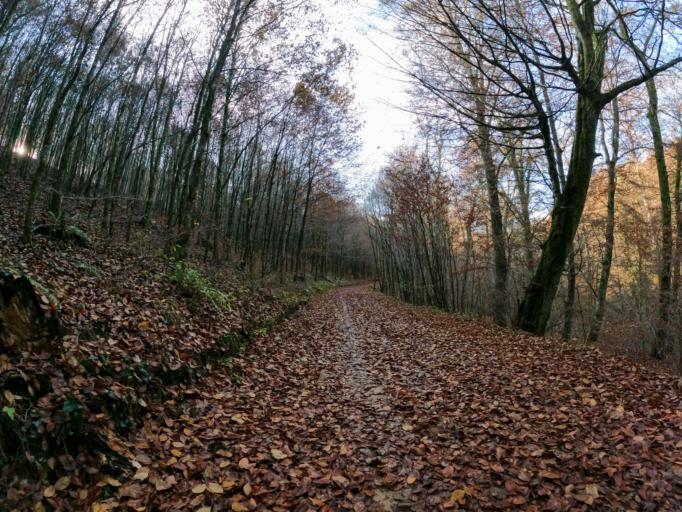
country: LU
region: Luxembourg
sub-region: Canton de Capellen
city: Mamer
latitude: 49.6436
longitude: 6.0304
